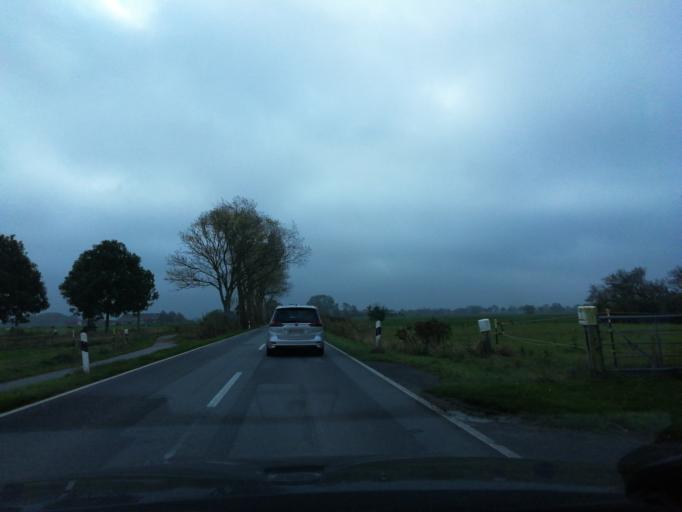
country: DE
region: Lower Saxony
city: Wangerooge
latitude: 53.6843
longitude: 7.8580
